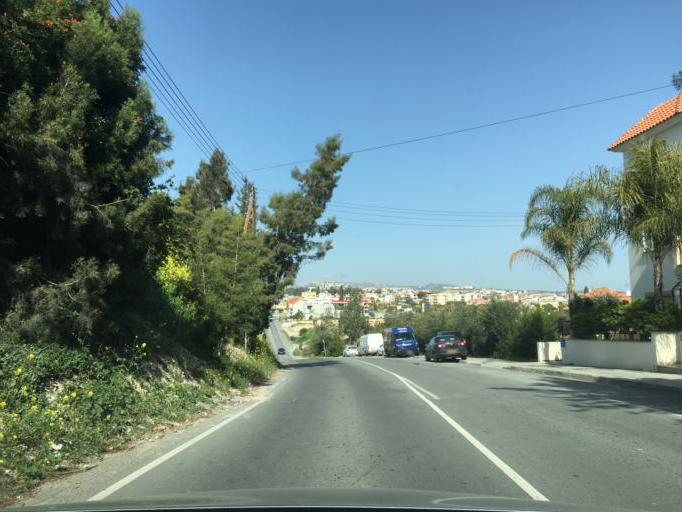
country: CY
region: Limassol
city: Pano Polemidia
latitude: 34.7025
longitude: 33.0020
